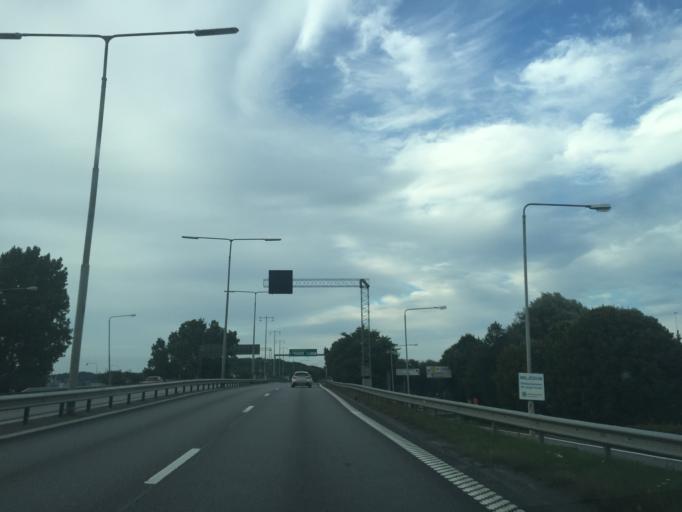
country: SE
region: Vaestra Goetaland
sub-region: Goteborg
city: Goeteborg
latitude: 57.7193
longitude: 11.9545
